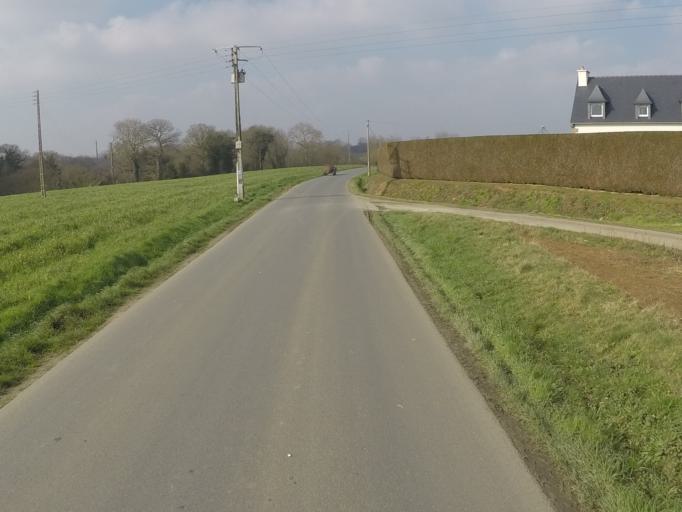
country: FR
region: Brittany
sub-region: Departement des Cotes-d'Armor
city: Goudelin
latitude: 48.6078
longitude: -3.0301
